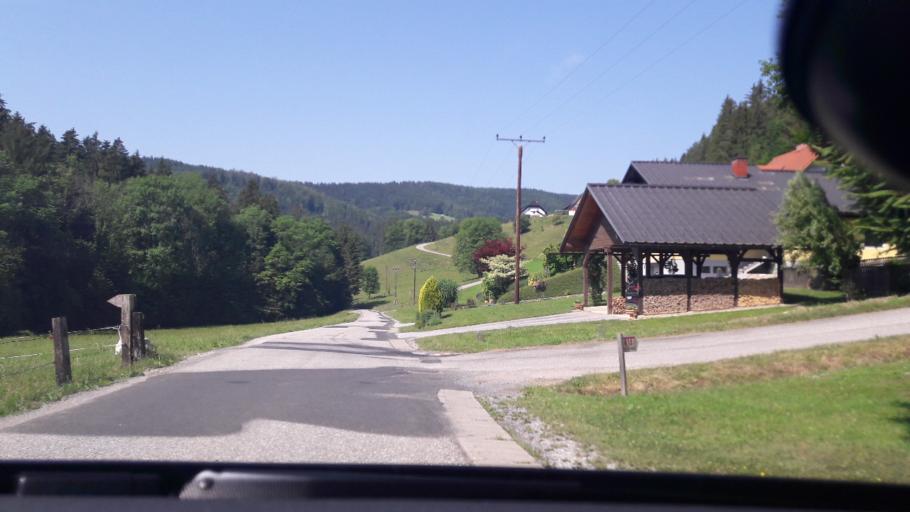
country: AT
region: Styria
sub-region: Politischer Bezirk Voitsberg
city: Sodingberg
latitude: 47.0986
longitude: 15.1901
